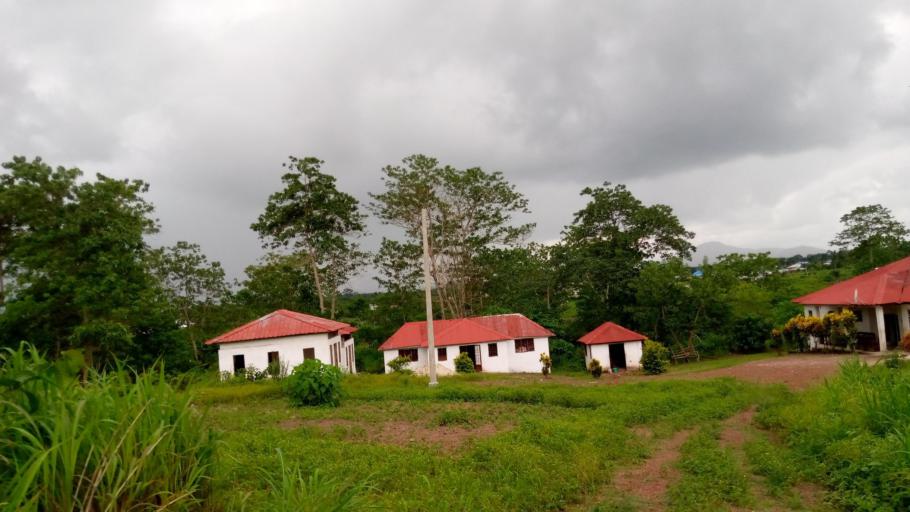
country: SL
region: Southern Province
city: Moyamba
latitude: 8.1586
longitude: -12.4418
